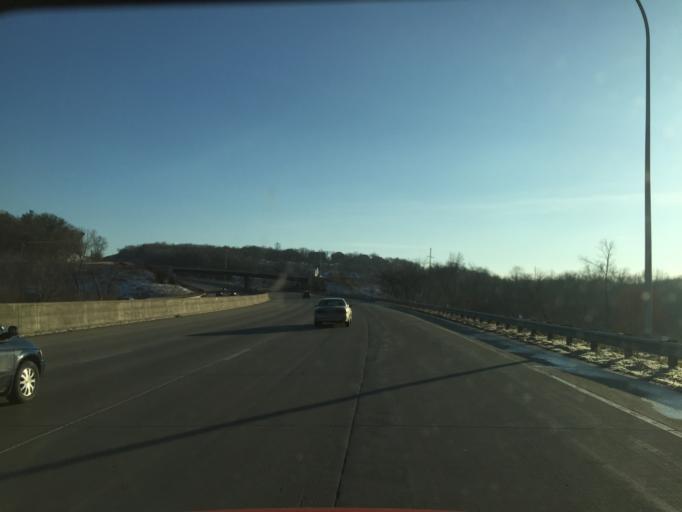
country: US
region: Minnesota
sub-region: Olmsted County
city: Rochester
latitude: 43.9970
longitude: -92.4851
